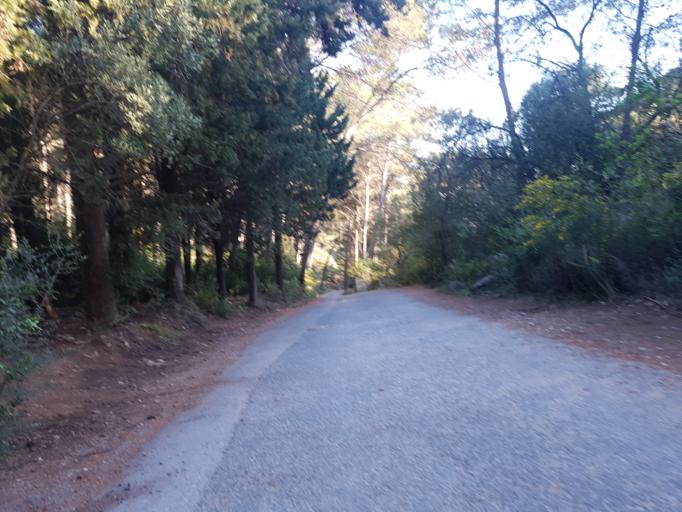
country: ES
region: Andalusia
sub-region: Provincia de Malaga
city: Marbella
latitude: 36.5340
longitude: -4.8844
